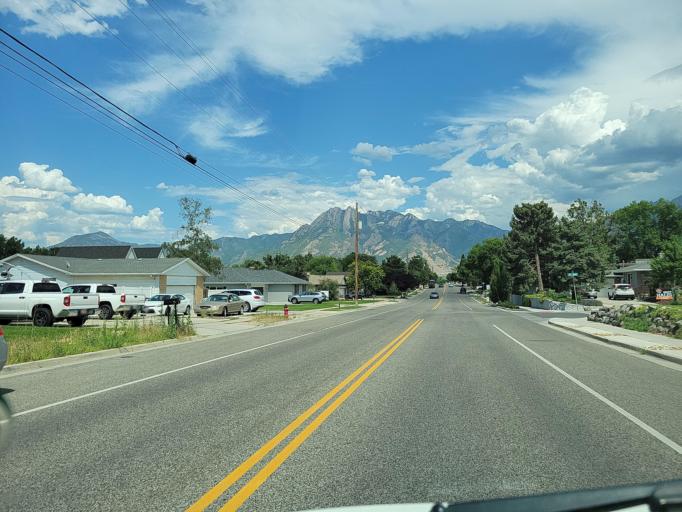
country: US
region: Utah
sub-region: Salt Lake County
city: Murray
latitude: 40.6417
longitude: -111.8759
